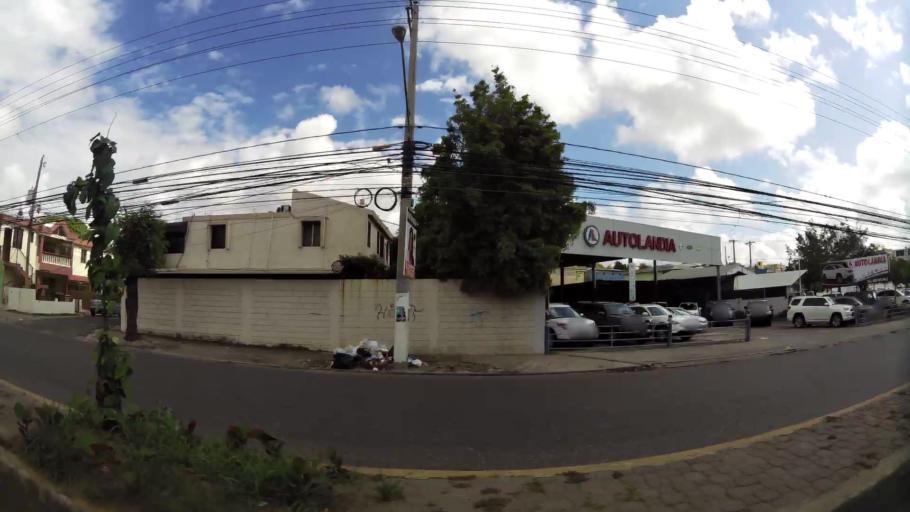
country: DO
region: Santiago
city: Santiago de los Caballeros
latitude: 19.4793
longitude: -70.7025
